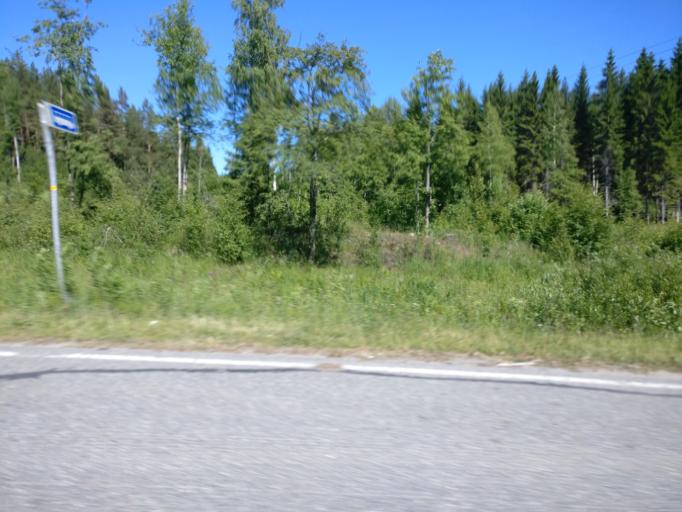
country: FI
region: Southern Savonia
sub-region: Savonlinna
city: Rantasalmi
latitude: 62.1281
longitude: 28.2586
